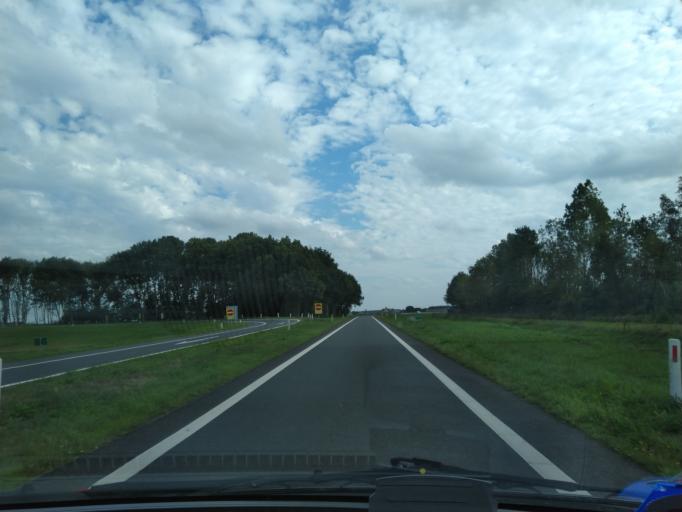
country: NL
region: Groningen
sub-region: Gemeente Haren
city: Haren
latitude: 53.1249
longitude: 6.6081
